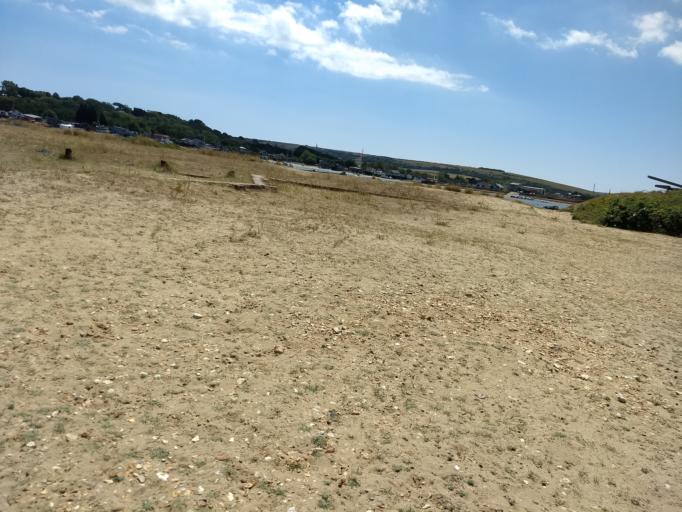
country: GB
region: England
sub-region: Isle of Wight
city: Bembridge
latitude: 50.6951
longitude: -1.0975
